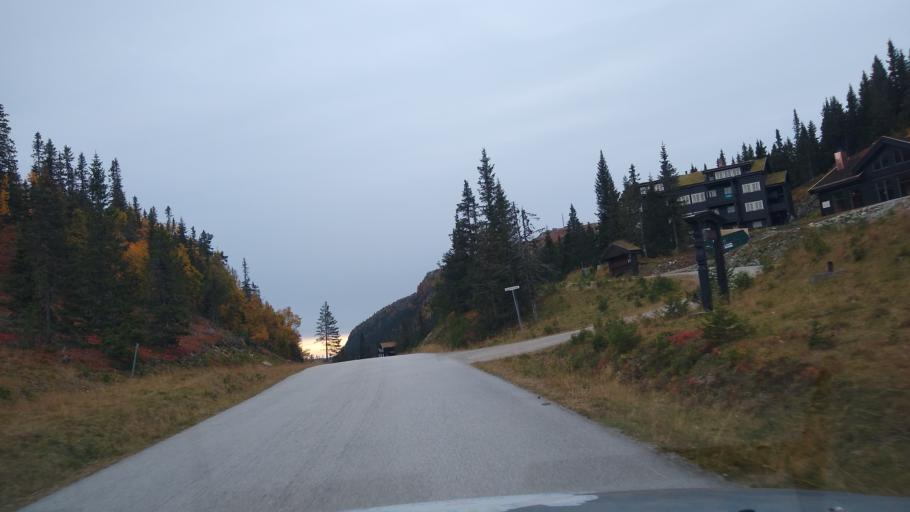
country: NO
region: Oppland
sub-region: Ringebu
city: Ringebu
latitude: 61.4788
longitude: 10.1252
